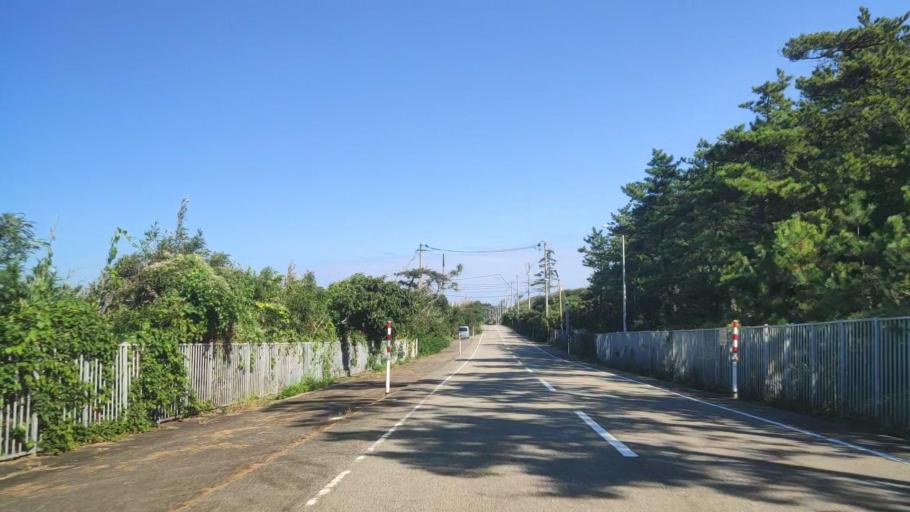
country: JP
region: Ishikawa
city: Hakui
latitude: 37.0632
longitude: 136.7231
